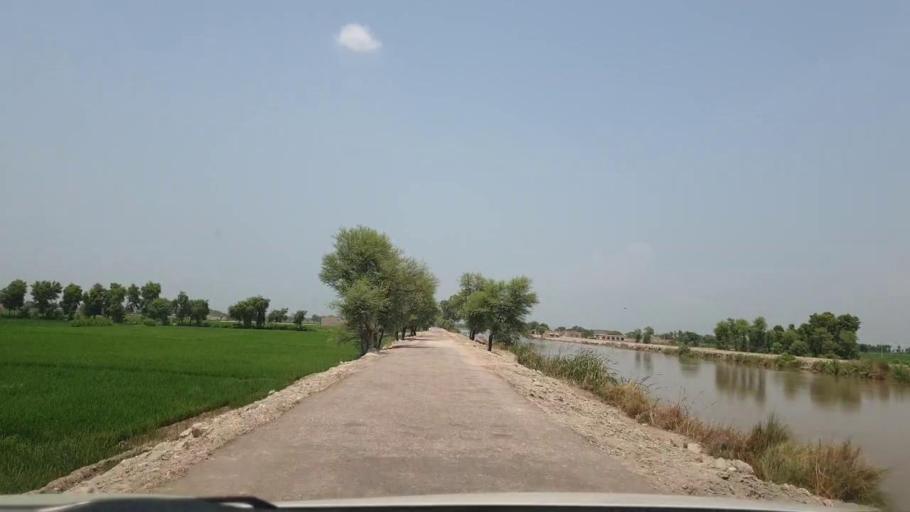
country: PK
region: Sindh
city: Dokri
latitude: 27.3326
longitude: 68.1097
